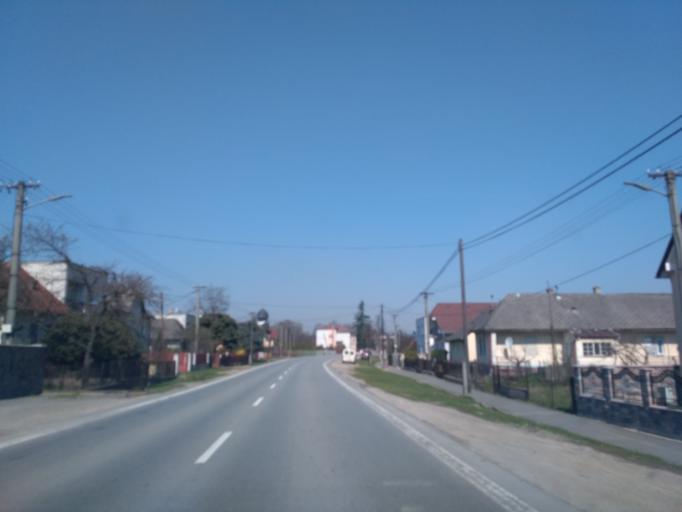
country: SK
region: Kosicky
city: Secovce
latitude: 48.7831
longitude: 21.6830
